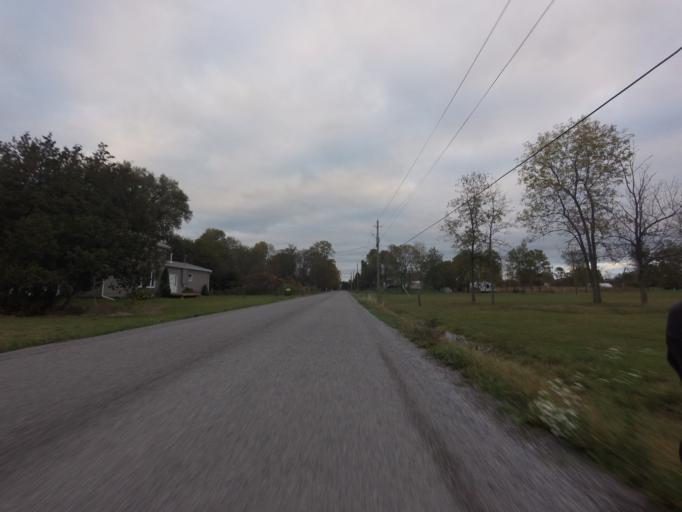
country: CA
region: Ontario
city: Quinte West
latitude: 44.0124
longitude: -77.7510
